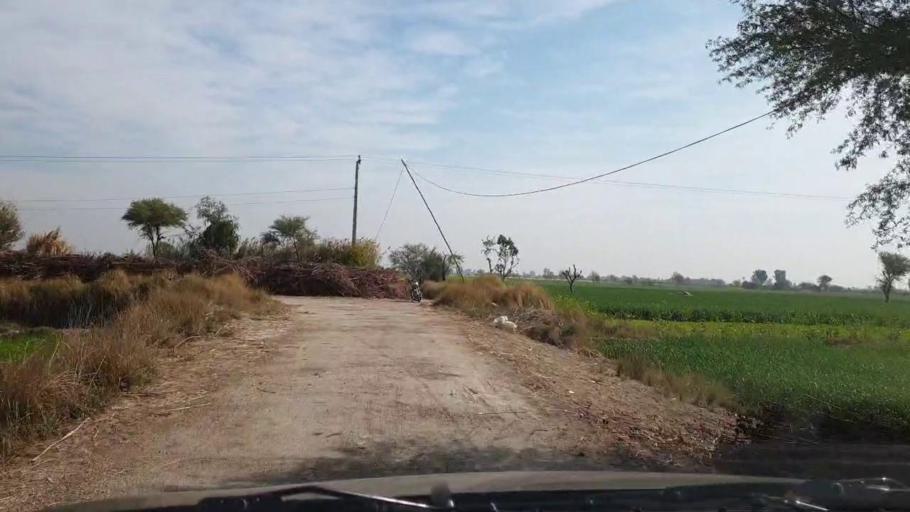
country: PK
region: Sindh
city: Jam Sahib
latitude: 26.2486
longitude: 68.6962
